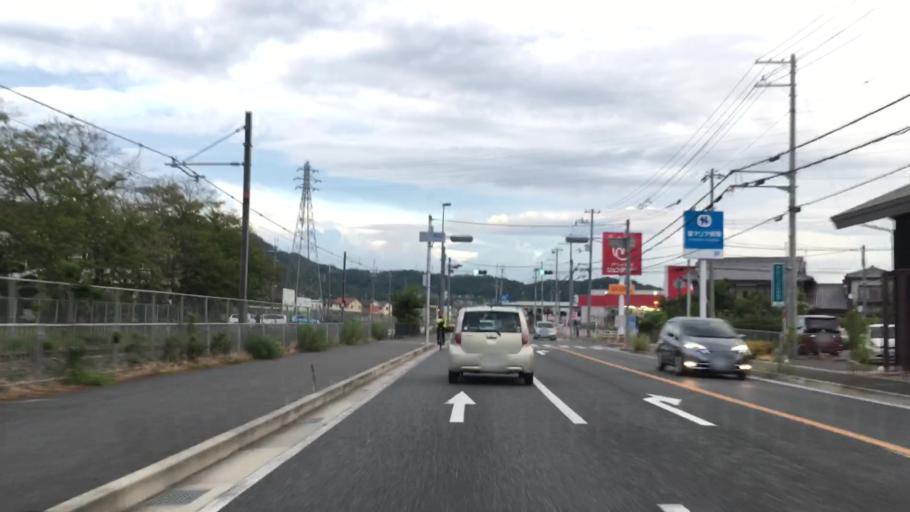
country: JP
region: Hyogo
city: Himeji
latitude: 34.8770
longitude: 134.7292
